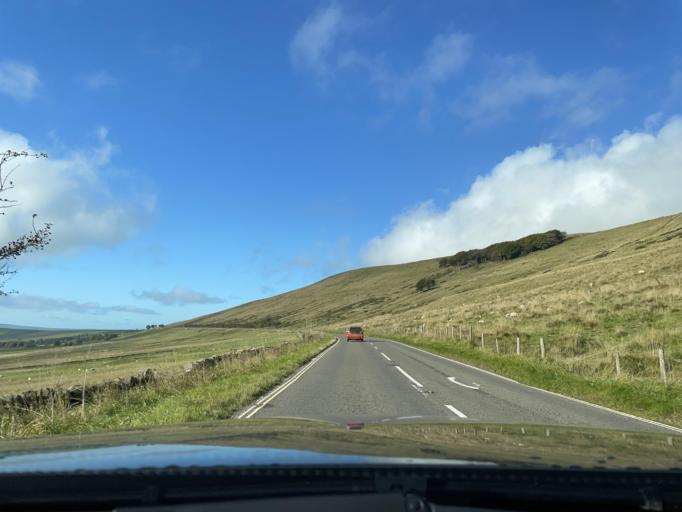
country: GB
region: England
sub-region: Derbyshire
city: High Peak
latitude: 53.3451
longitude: -1.8213
